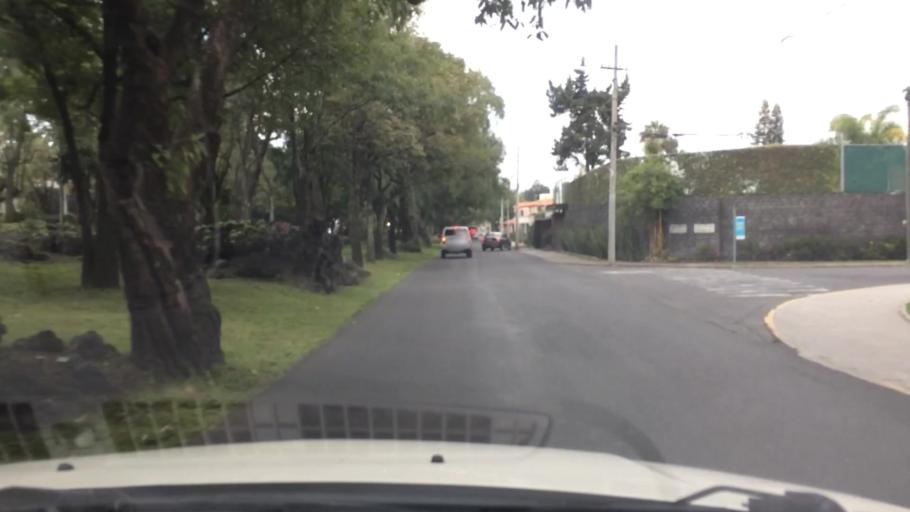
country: MX
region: Mexico City
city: Magdalena Contreras
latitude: 19.3116
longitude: -99.2104
